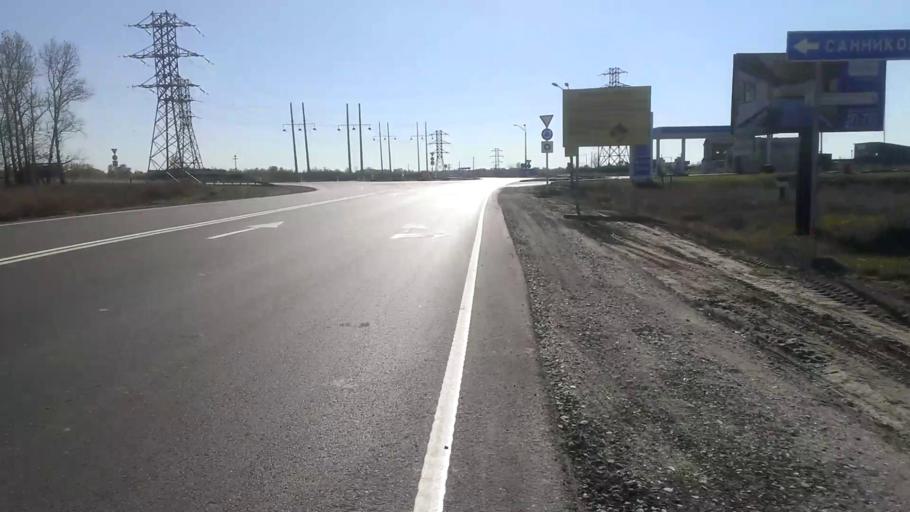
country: RU
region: Altai Krai
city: Sannikovo
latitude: 53.3375
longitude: 83.9385
